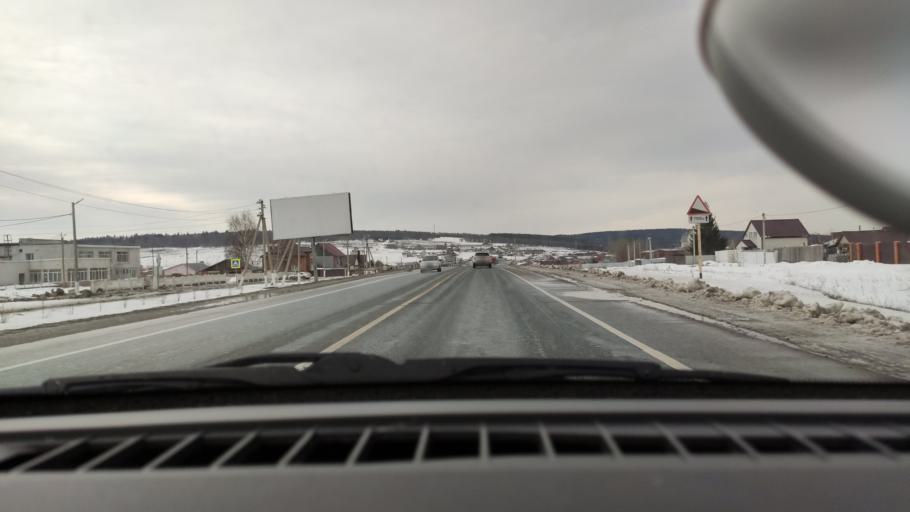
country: RU
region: Samara
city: Kurumoch
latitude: 53.4836
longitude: 50.0333
